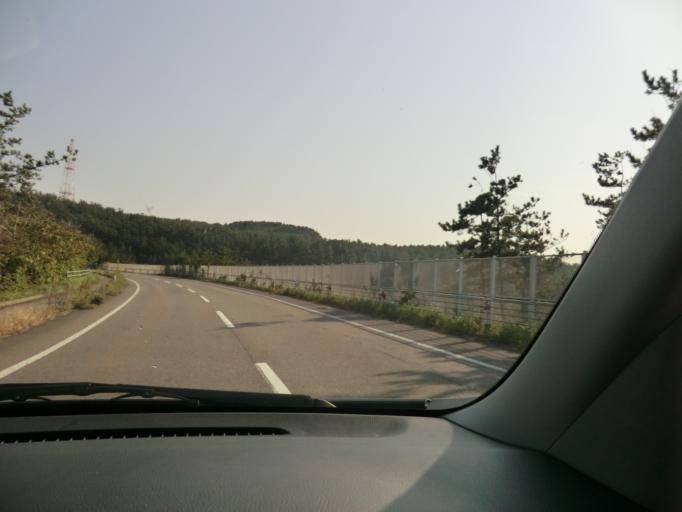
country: JP
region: Niigata
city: Kashiwazaki
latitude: 37.4454
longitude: 138.6054
